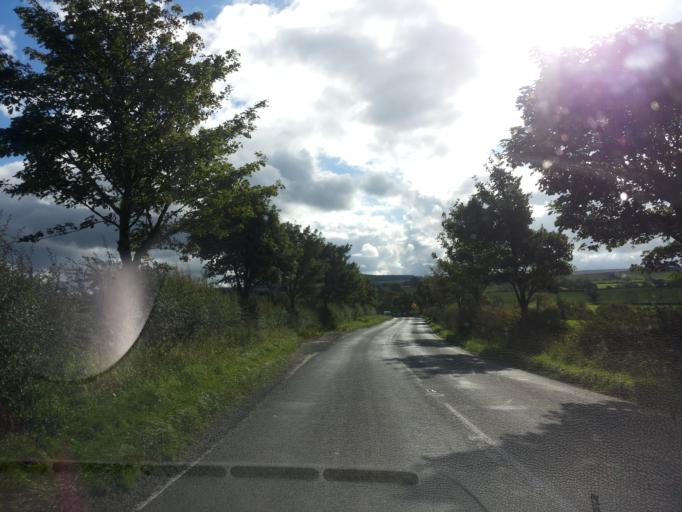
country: GB
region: England
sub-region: North Yorkshire
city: Leyburn
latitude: 54.2973
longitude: -1.8207
